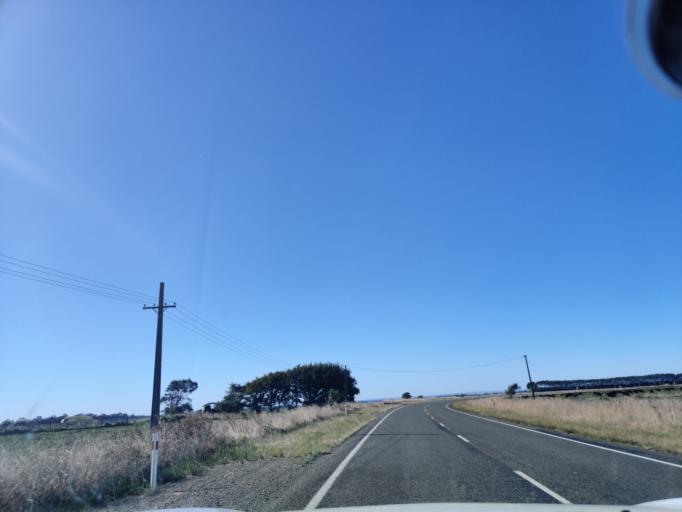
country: NZ
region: Manawatu-Wanganui
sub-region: Palmerston North City
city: Palmerston North
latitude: -40.4166
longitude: 175.4742
